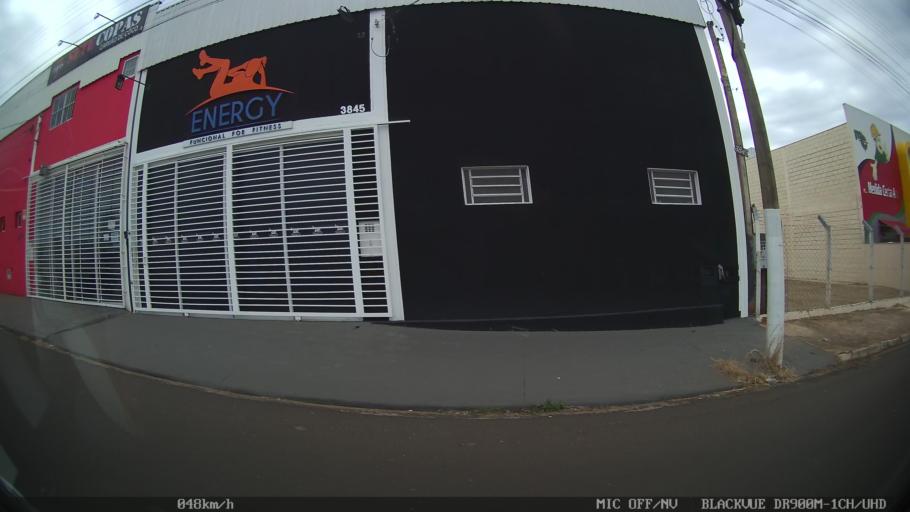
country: BR
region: Sao Paulo
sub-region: Sao Jose Do Rio Preto
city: Sao Jose do Rio Preto
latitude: -20.8152
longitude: -49.4925
